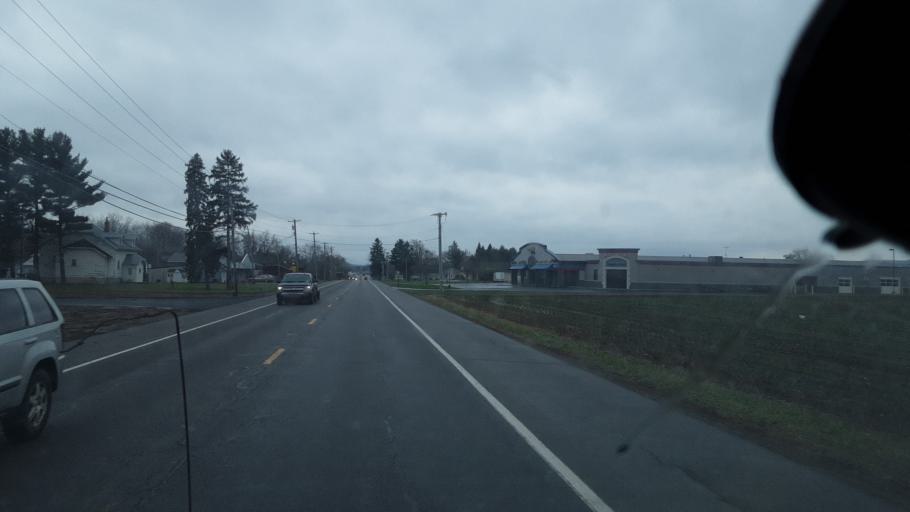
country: US
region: New York
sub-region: Cattaraugus County
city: Yorkshire
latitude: 42.5480
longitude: -78.4782
